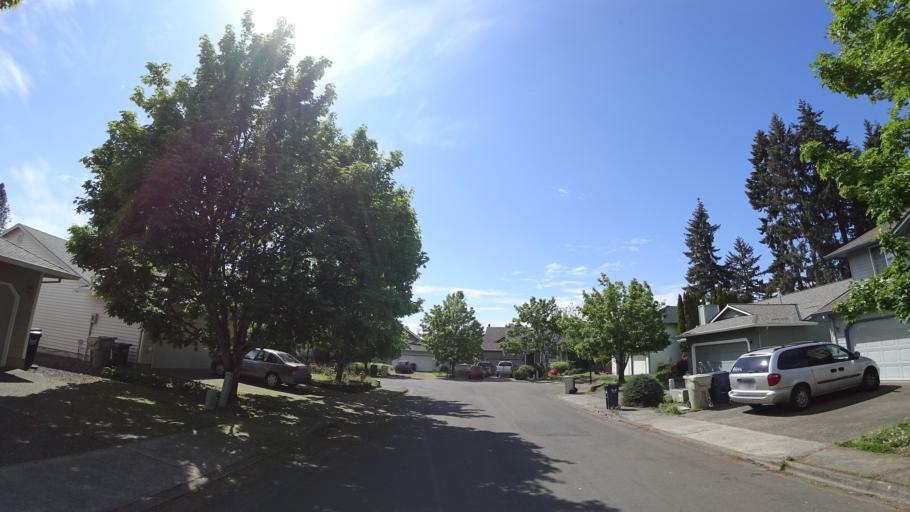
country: US
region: Oregon
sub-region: Washington County
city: Aloha
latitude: 45.4902
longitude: -122.8893
